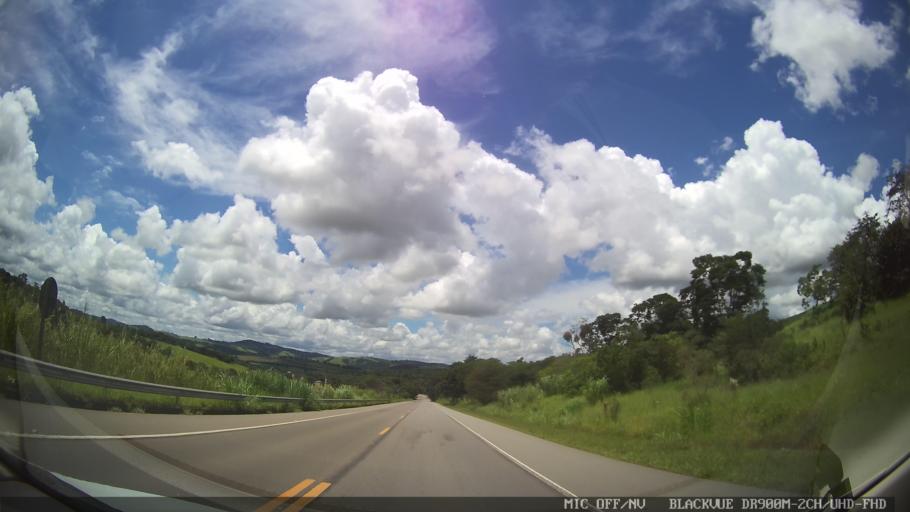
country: BR
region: Sao Paulo
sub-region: Amparo
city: Amparo
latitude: -22.8054
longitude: -46.7153
